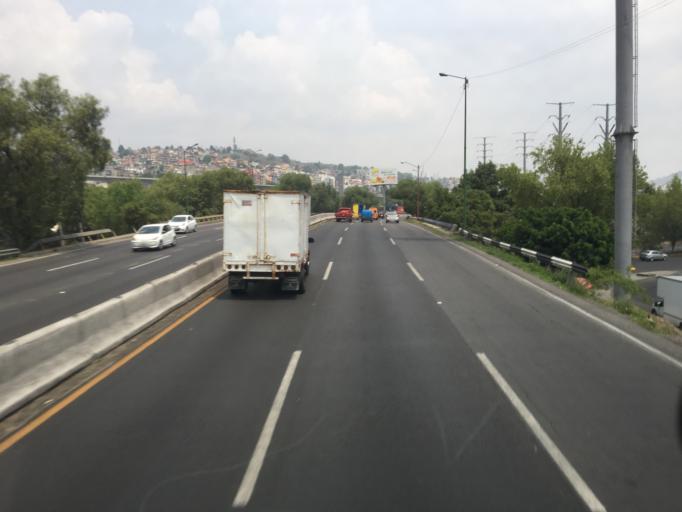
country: MX
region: Mexico
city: Tlalnepantla
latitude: 19.5628
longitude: -99.2026
